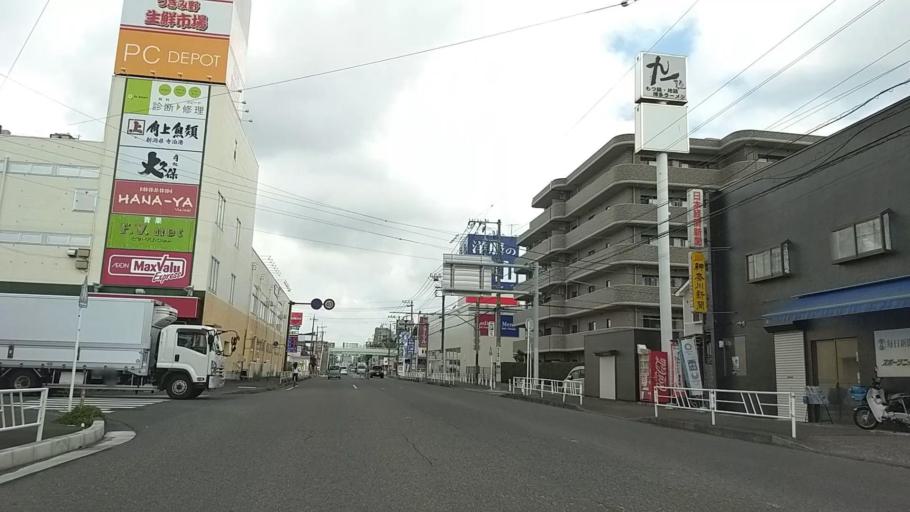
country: JP
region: Kanagawa
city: Minami-rinkan
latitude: 35.5070
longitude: 139.4625
